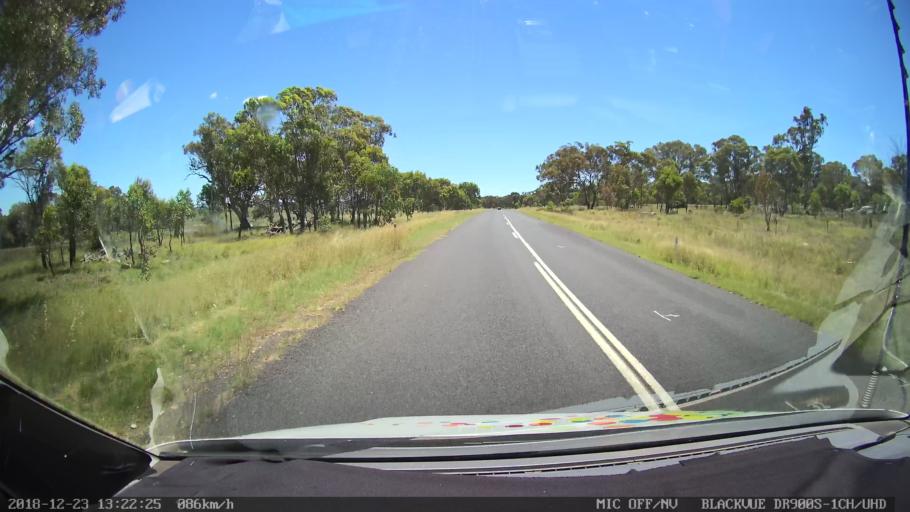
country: AU
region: New South Wales
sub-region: Armidale Dumaresq
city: Armidale
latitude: -30.4794
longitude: 151.4213
